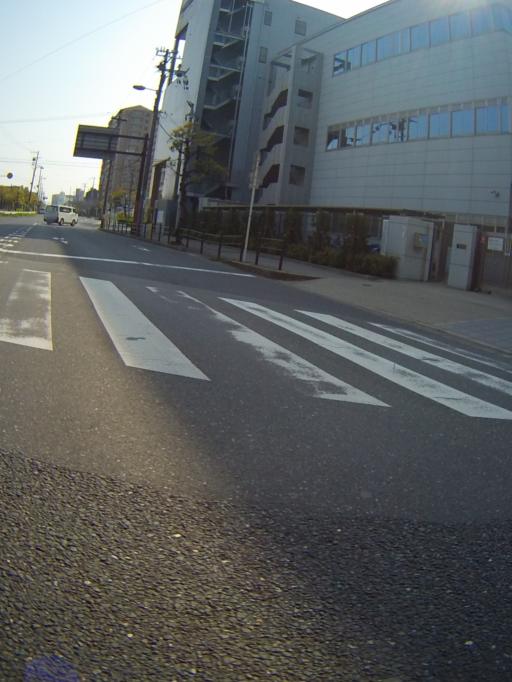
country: JP
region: Osaka
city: Osaka-shi
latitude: 34.6583
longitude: 135.4684
